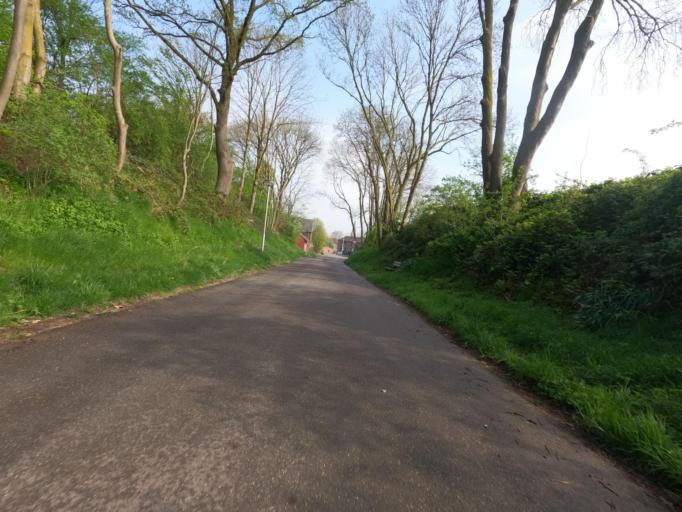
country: DE
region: North Rhine-Westphalia
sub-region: Regierungsbezirk Koln
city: Heinsberg
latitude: 51.0467
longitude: 6.1253
